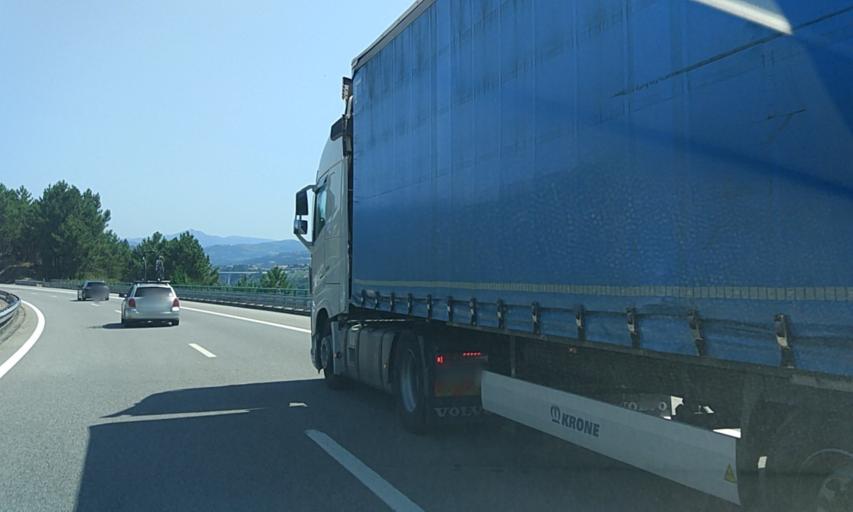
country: PT
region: Porto
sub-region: Amarante
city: Figueiro
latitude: 41.2539
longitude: -8.1382
